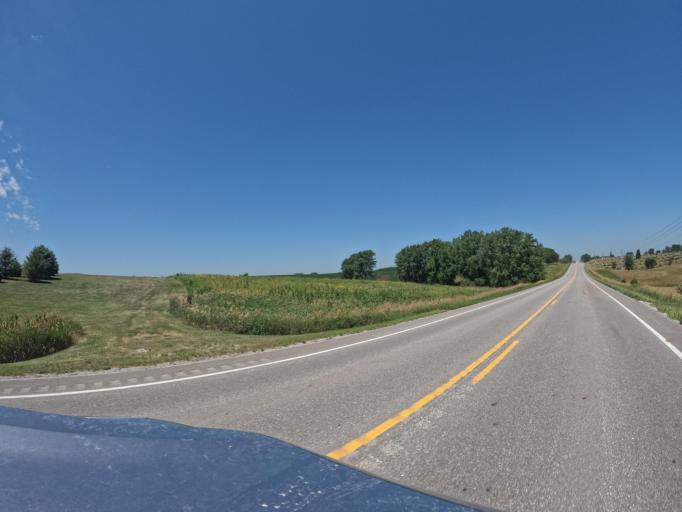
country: US
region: Iowa
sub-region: Keokuk County
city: Sigourney
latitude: 41.4595
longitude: -92.3551
